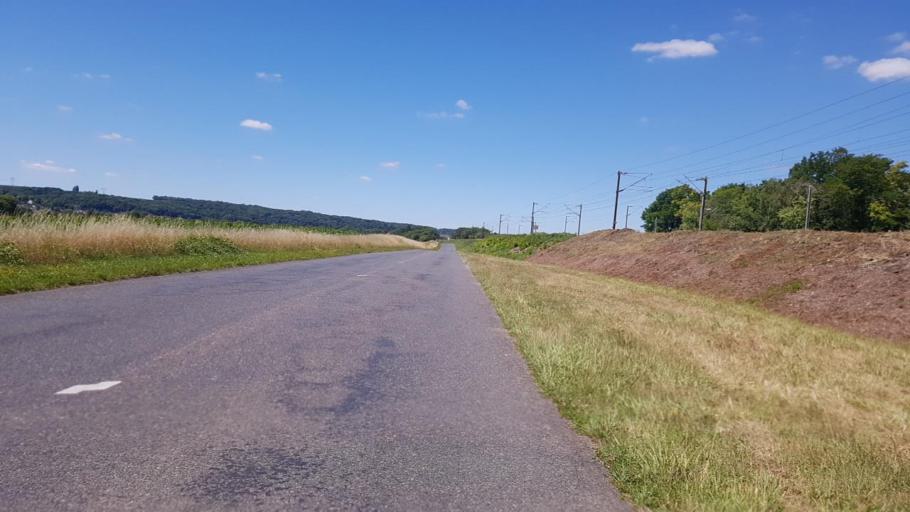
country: FR
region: Ile-de-France
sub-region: Departement de Seine-et-Marne
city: Changis-sur-Marne
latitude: 48.9592
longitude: 3.0443
